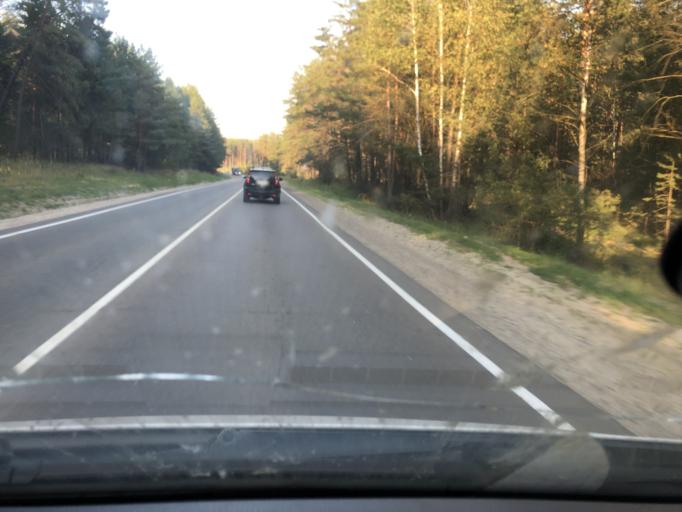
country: RU
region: Kaluga
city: Peremyshl'
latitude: 54.3526
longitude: 36.1982
